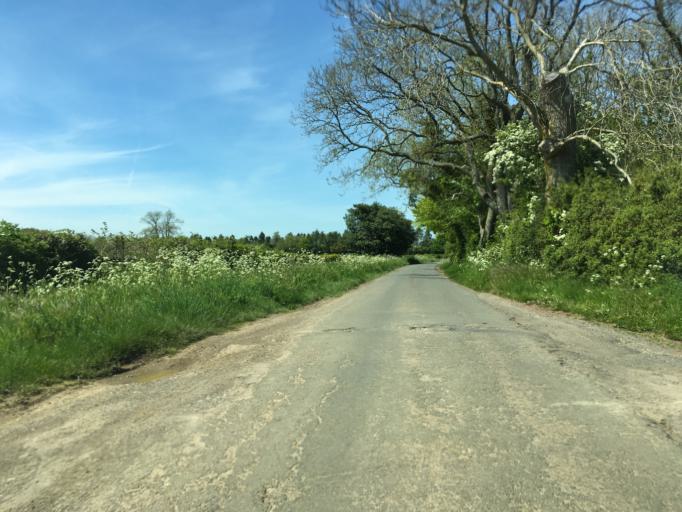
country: GB
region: England
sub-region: Gloucestershire
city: Coates
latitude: 51.6820
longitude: -1.9977
